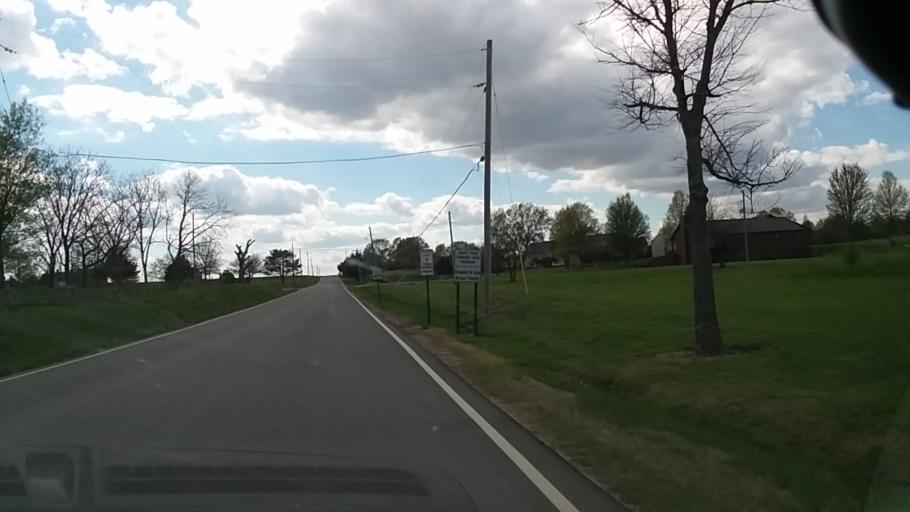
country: US
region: Kansas
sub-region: Douglas County
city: Lawrence
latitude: 38.8992
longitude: -95.2420
